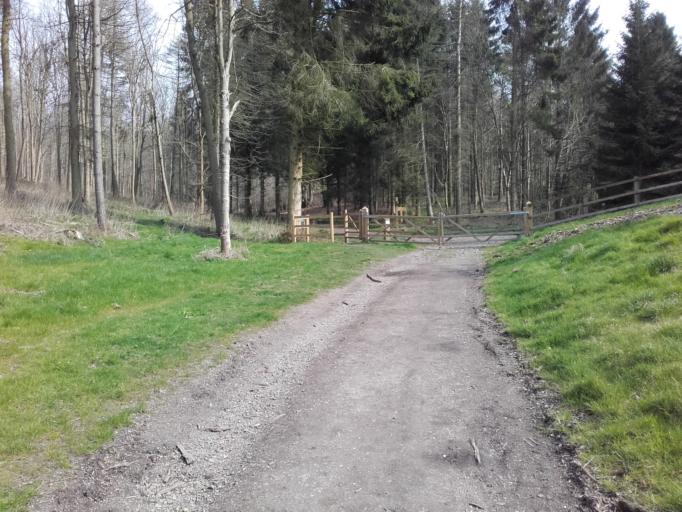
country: GB
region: England
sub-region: East Riding of Yorkshire
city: South Cave
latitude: 53.7932
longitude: -0.5707
